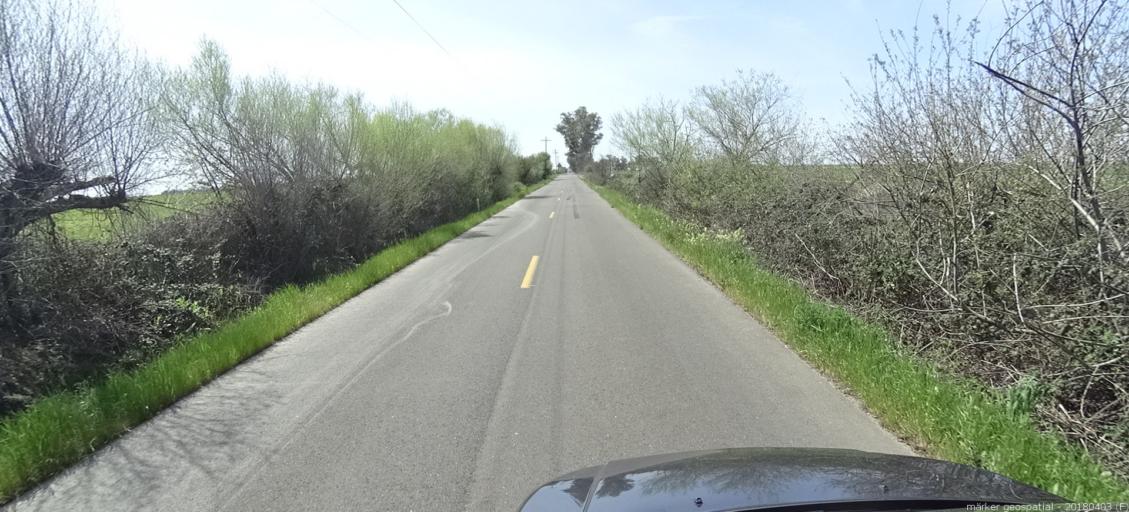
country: US
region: California
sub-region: Sacramento County
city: Herald
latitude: 38.3362
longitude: -121.2718
